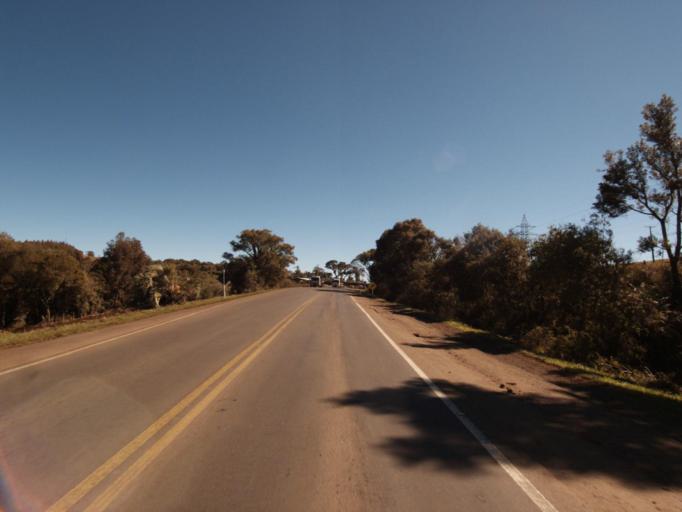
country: BR
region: Santa Catarina
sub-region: Concordia
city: Concordia
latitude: -26.8931
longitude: -51.9817
